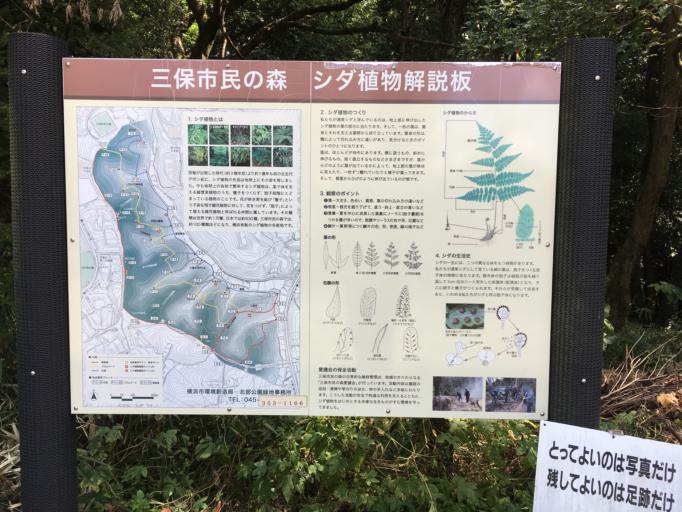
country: JP
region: Kanagawa
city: Minami-rinkan
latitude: 35.5039
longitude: 139.5061
